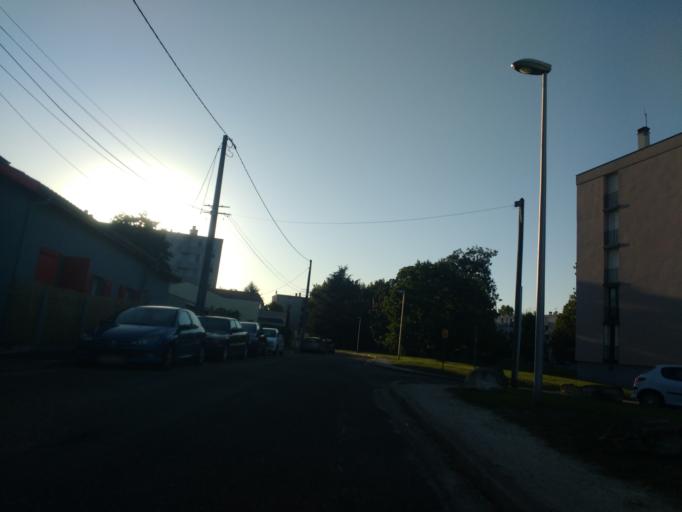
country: FR
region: Aquitaine
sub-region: Departement de la Gironde
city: Pessac
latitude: 44.8140
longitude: -0.6296
